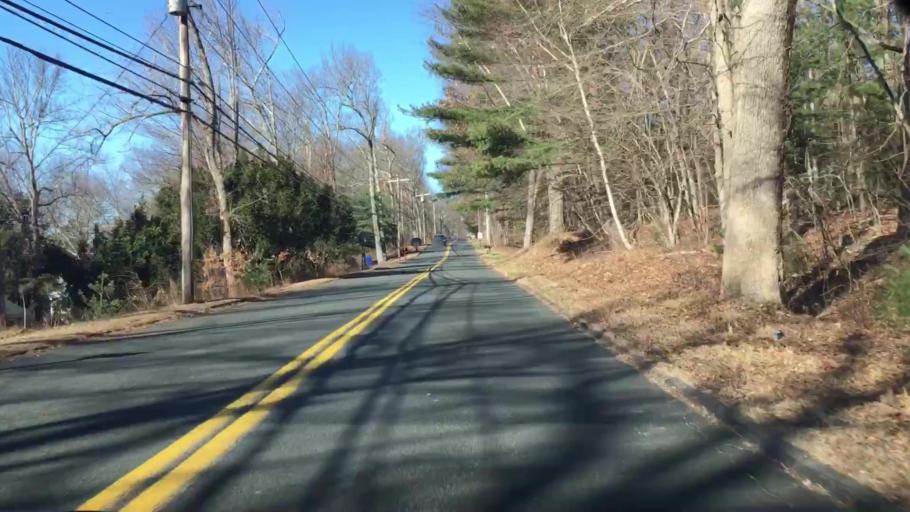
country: US
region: Connecticut
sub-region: Tolland County
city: Crystal Lake
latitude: 41.9337
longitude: -72.3865
